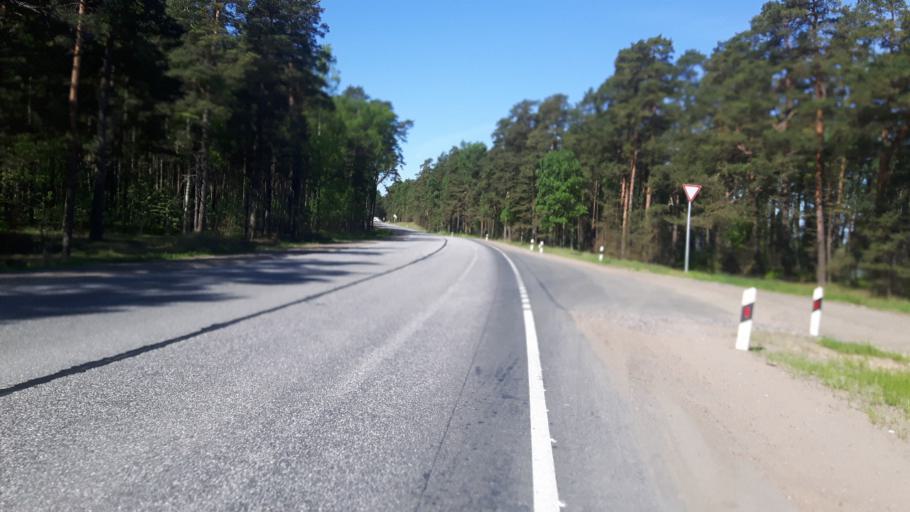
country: RU
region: Leningrad
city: Lebyazh'ye
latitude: 59.9570
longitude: 29.4654
